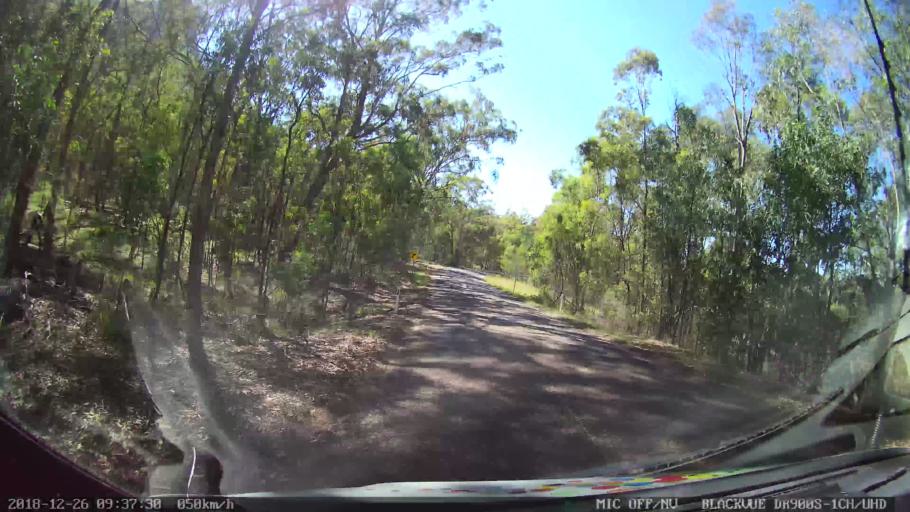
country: AU
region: New South Wales
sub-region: Mid-Western Regional
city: Kandos
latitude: -32.9328
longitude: 150.0405
